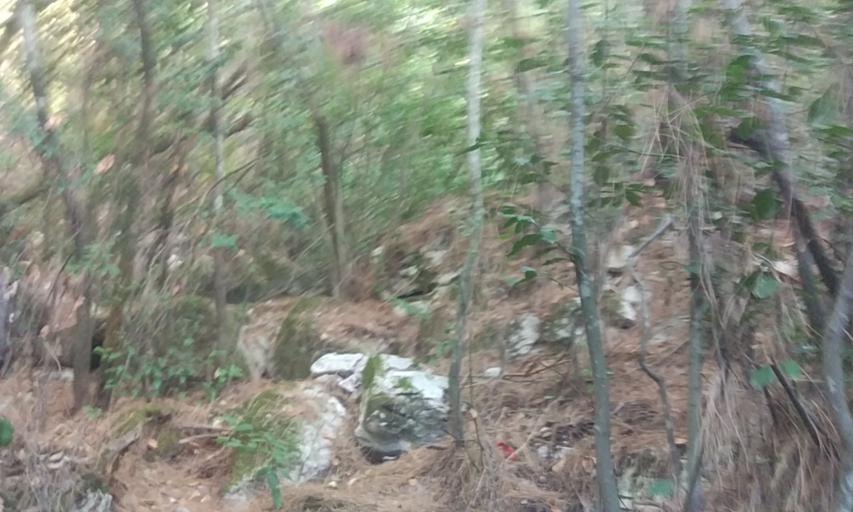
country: TR
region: Antalya
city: Tekirova
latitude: 36.3803
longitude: 30.4765
